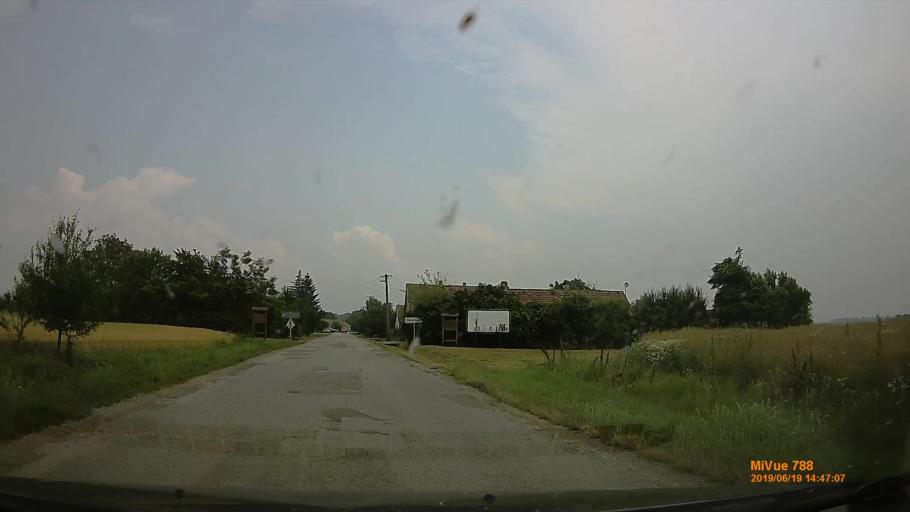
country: HU
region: Baranya
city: Szigetvar
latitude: 45.9989
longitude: 17.8285
